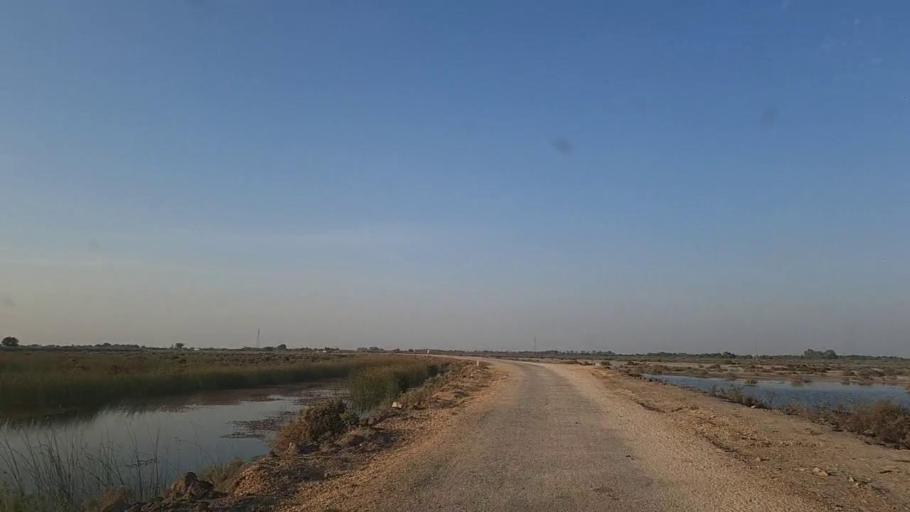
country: PK
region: Sindh
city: Mirpur Batoro
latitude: 24.6874
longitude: 68.2035
